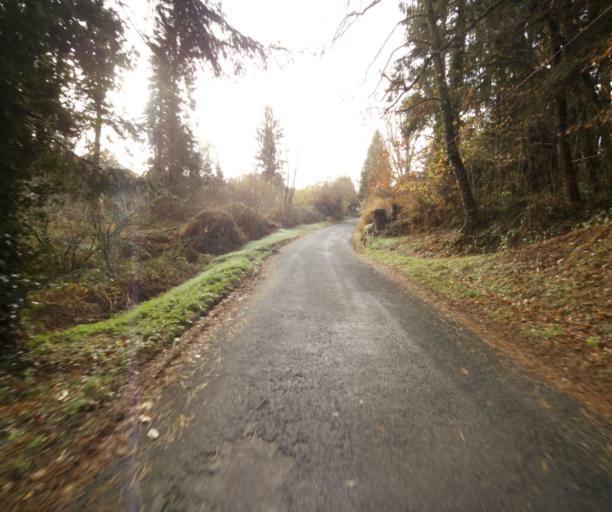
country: FR
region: Limousin
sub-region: Departement de la Correze
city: Cornil
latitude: 45.2143
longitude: 1.7139
